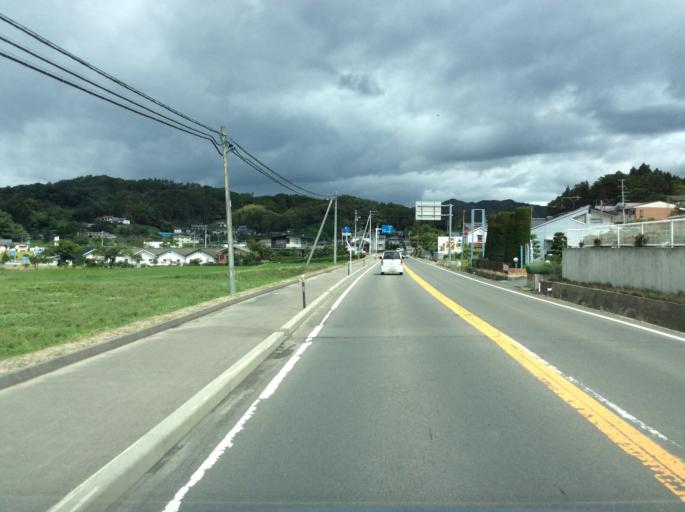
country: JP
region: Fukushima
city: Fukushima-shi
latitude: 37.6727
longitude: 140.5674
